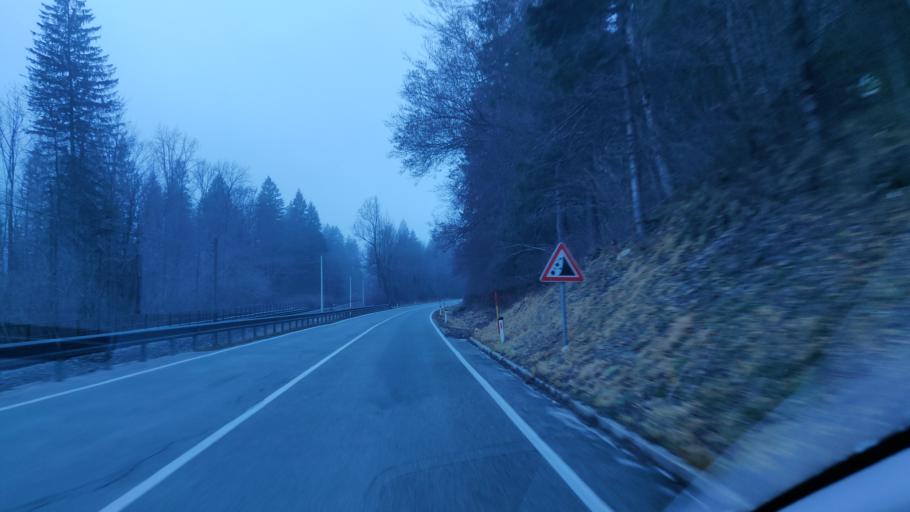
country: SI
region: Bohinj
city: Bohinjska Bistrica
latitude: 46.2896
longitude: 14.0312
